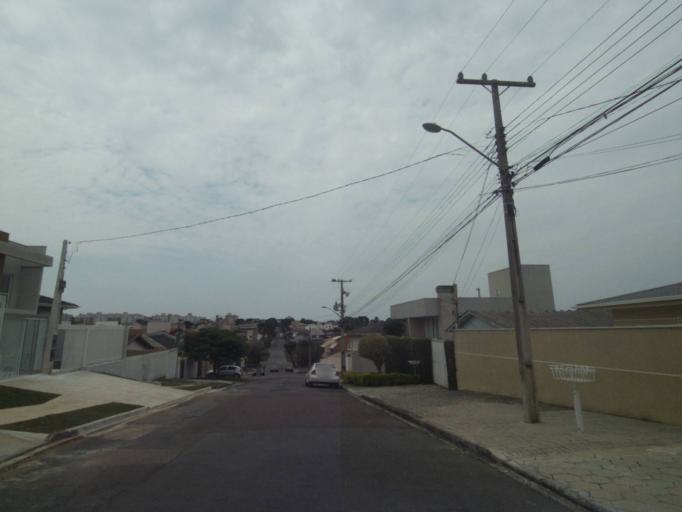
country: BR
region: Parana
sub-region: Curitiba
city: Curitiba
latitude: -25.4652
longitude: -49.3057
